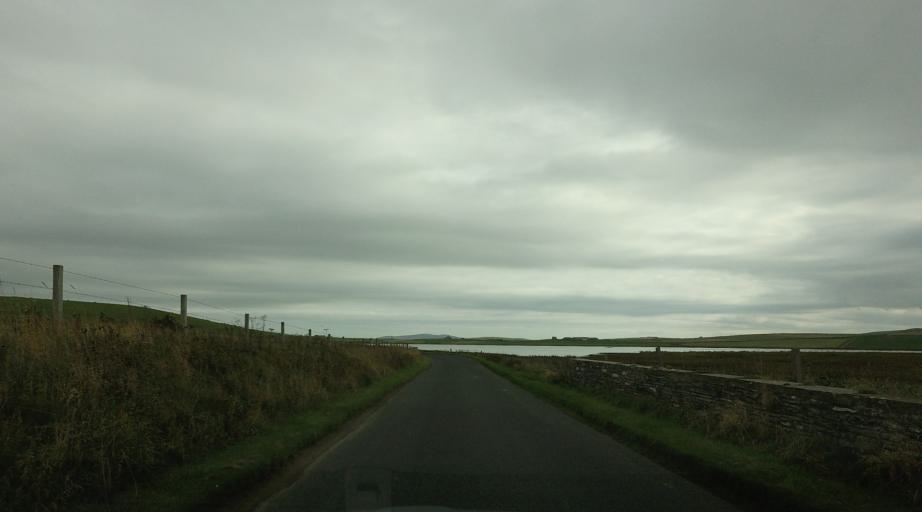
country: GB
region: Scotland
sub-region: Orkney Islands
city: Stromness
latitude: 59.0483
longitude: -3.3281
